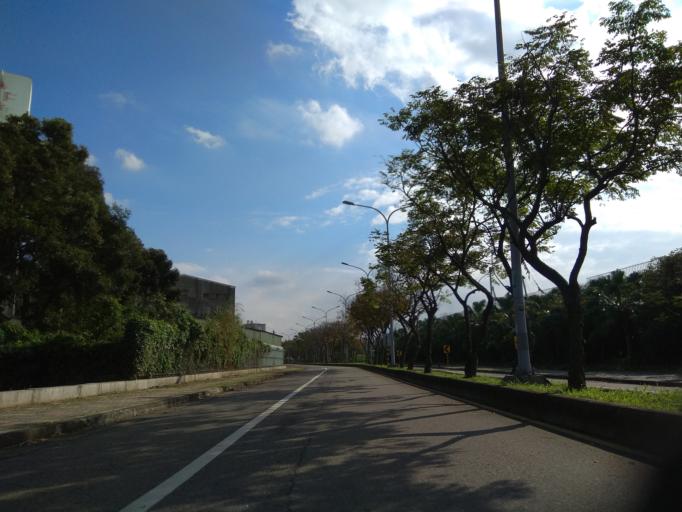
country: TW
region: Taiwan
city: Taoyuan City
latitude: 25.0580
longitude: 121.1799
